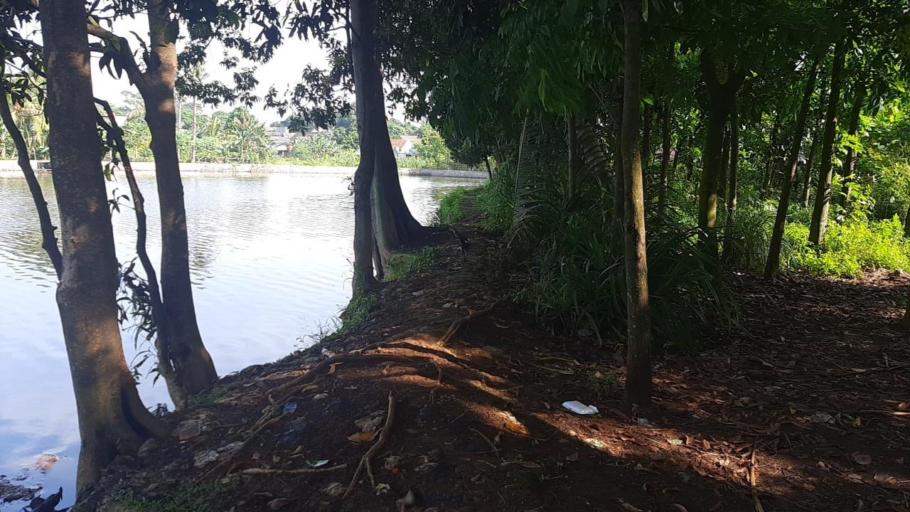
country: ID
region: West Java
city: Citeureup
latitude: -6.4529
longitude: 106.8925
